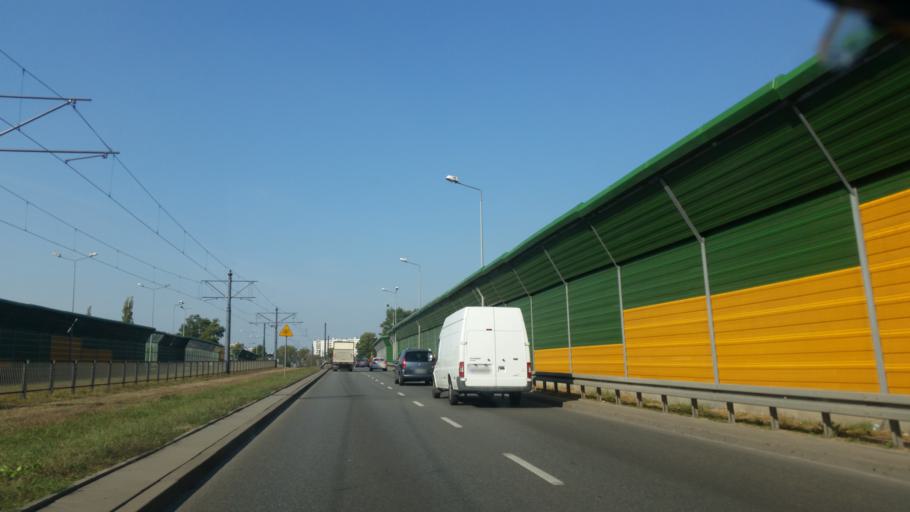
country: PL
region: Masovian Voivodeship
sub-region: Warszawa
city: Bemowo
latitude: 52.2447
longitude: 20.9122
